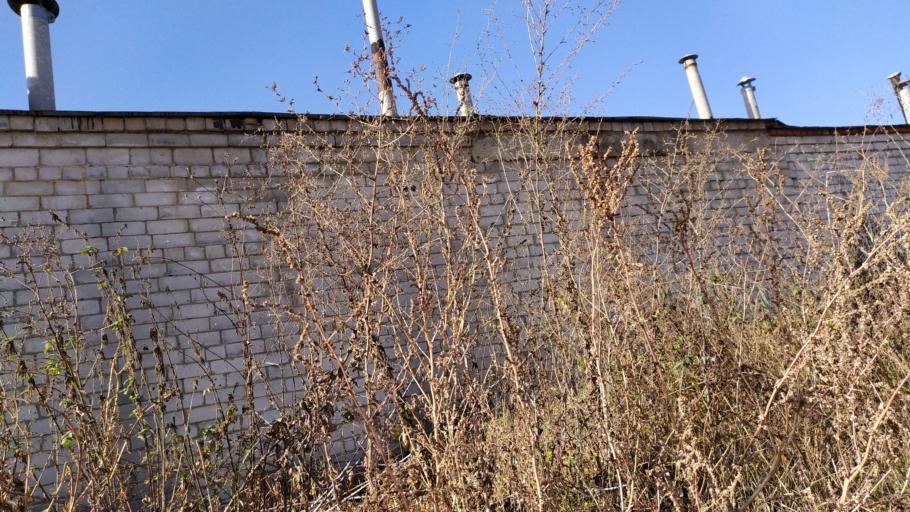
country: RU
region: Kursk
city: Kursk
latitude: 51.6511
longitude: 36.1528
